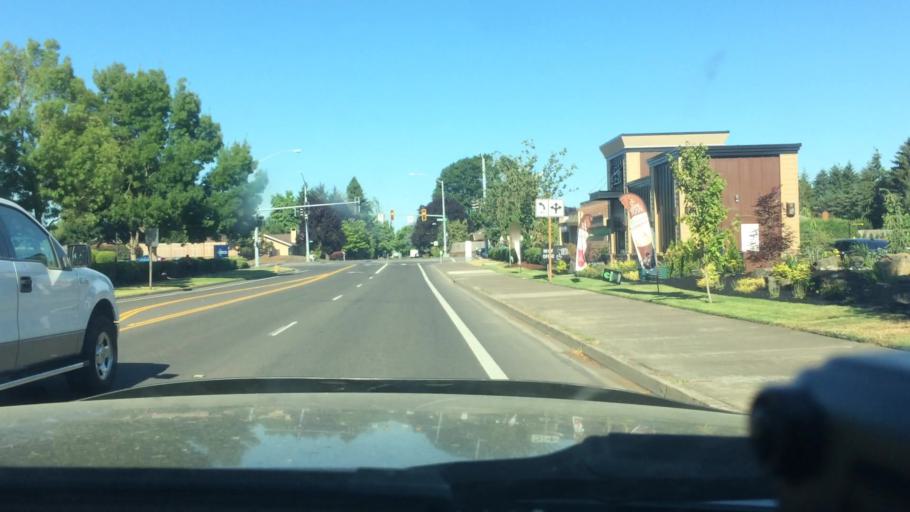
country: US
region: Oregon
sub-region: Lane County
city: Eugene
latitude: 44.0902
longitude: -123.0664
